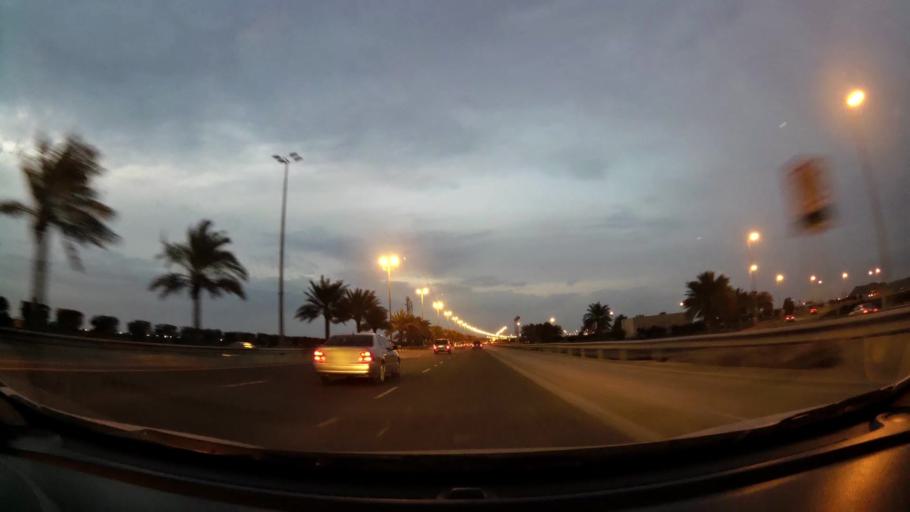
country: BH
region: Northern
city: Madinat `Isa
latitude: 26.1633
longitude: 50.5041
